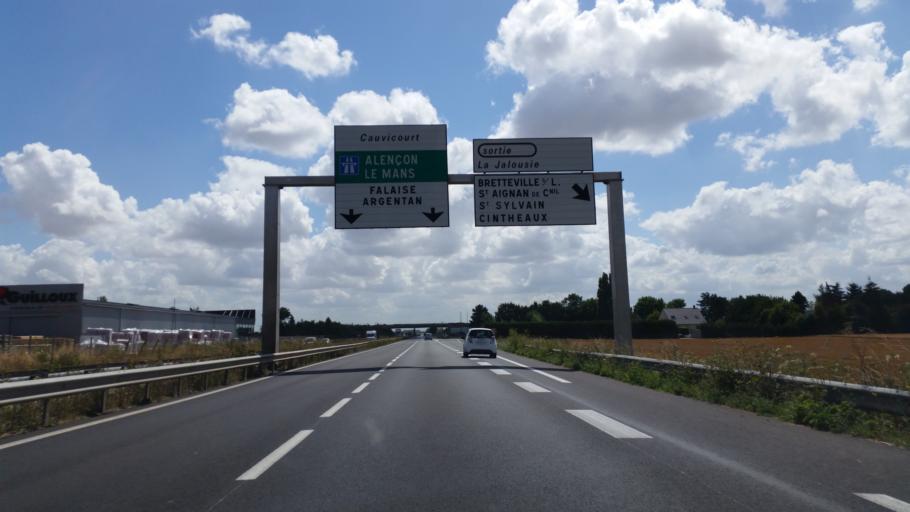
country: FR
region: Lower Normandy
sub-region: Departement du Calvados
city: Bretteville-sur-Laize
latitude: 49.0763
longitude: -0.2991
